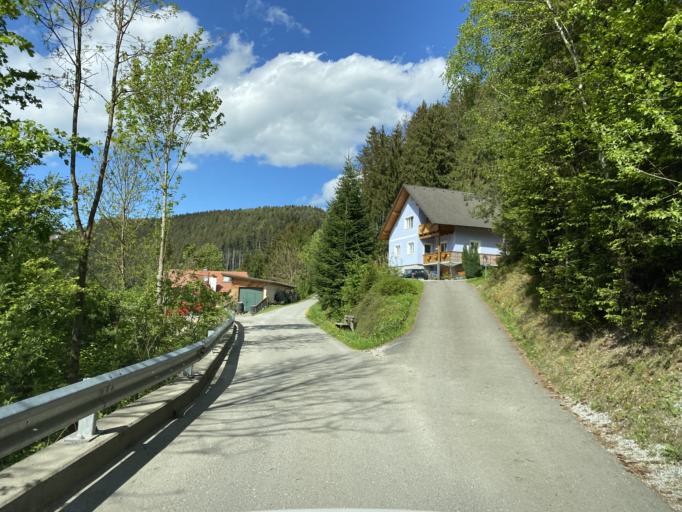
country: AT
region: Styria
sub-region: Politischer Bezirk Weiz
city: Birkfeld
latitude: 47.3509
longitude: 15.7008
